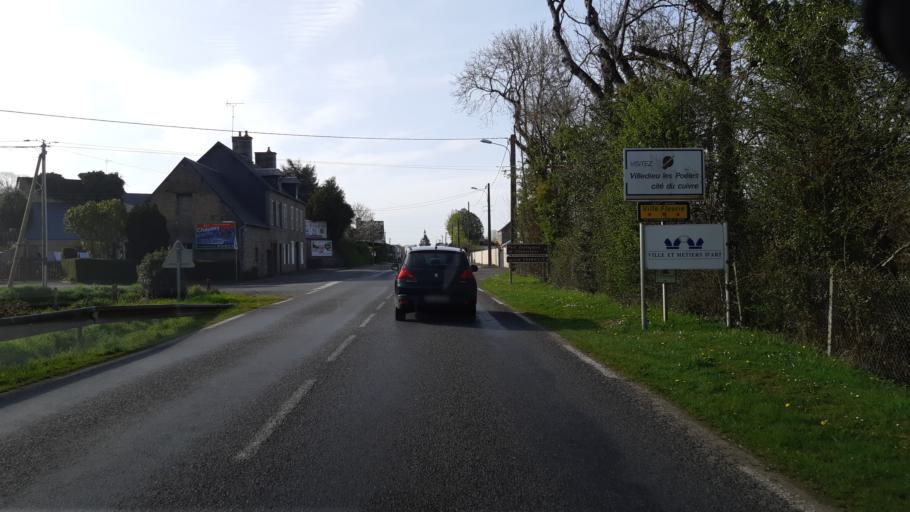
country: FR
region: Lower Normandy
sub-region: Departement de la Manche
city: Villedieu-les-Poeles
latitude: 48.8328
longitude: -1.2157
